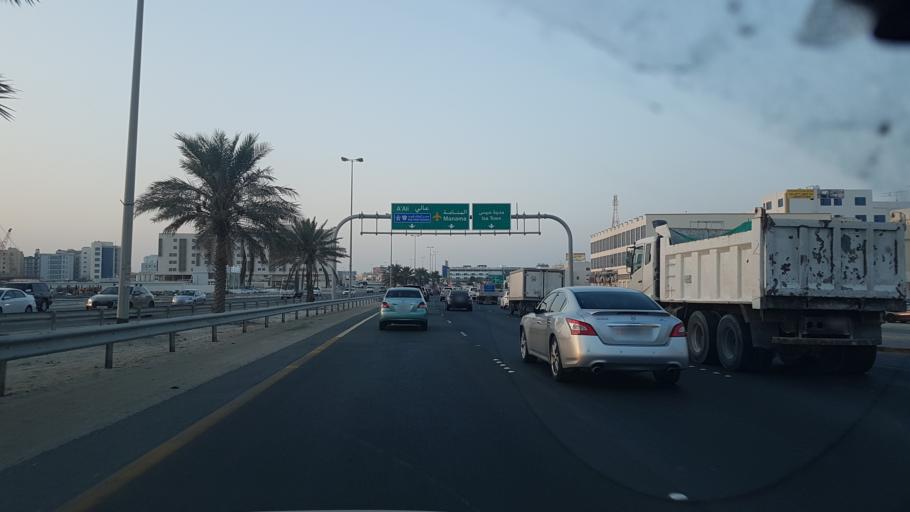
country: BH
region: Northern
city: Ar Rifa'
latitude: 26.1458
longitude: 50.5772
